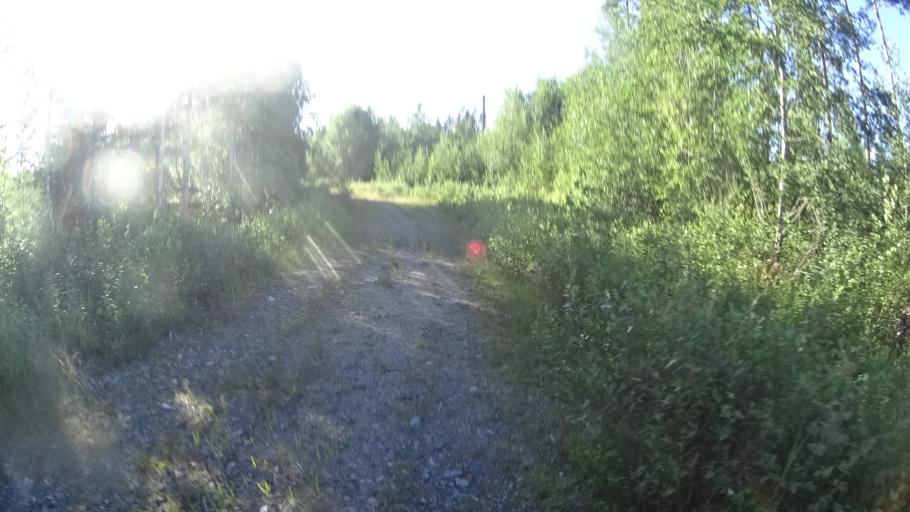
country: FI
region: Uusimaa
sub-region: Helsinki
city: Karkkila
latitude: 60.6548
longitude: 24.1396
